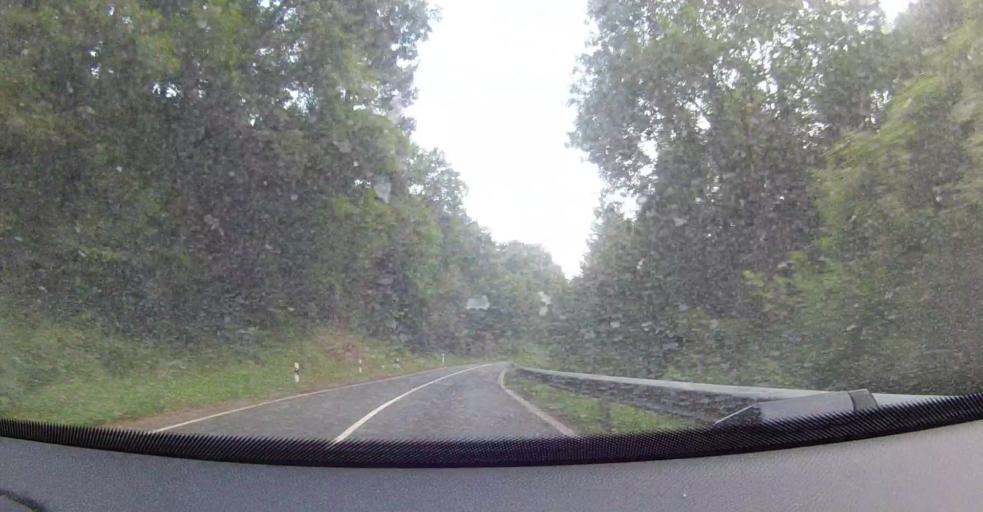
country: ES
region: Basque Country
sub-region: Bizkaia
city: Urrestieta
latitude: 43.2399
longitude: -3.1574
